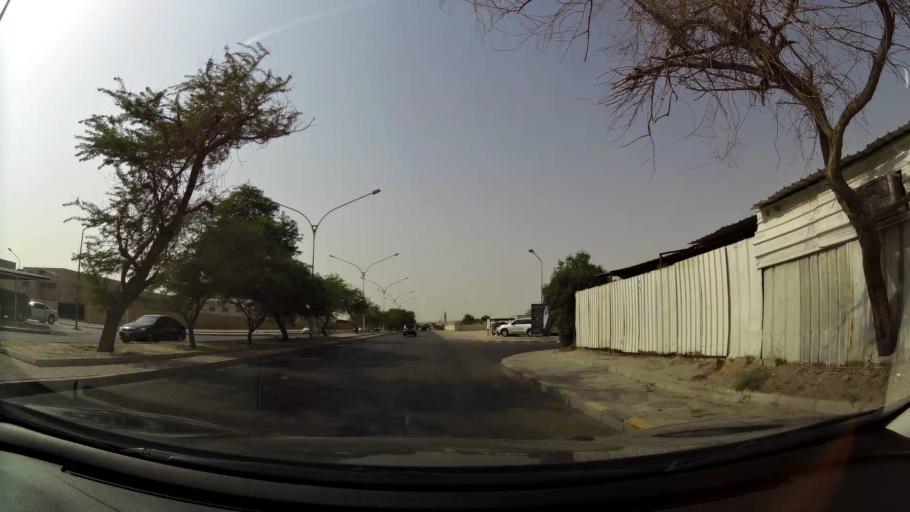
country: KW
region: Muhafazat al Jahra'
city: Al Jahra'
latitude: 29.3296
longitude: 47.6787
